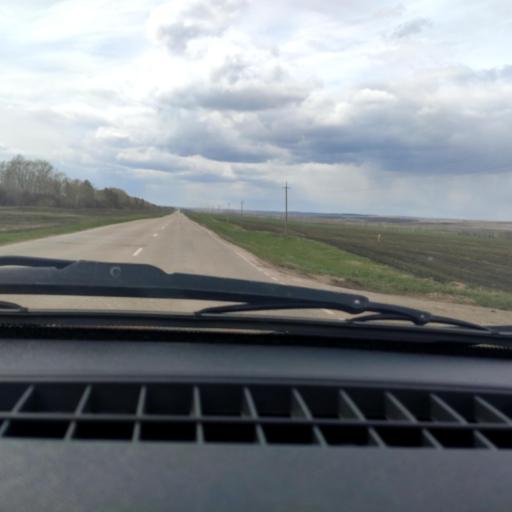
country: RU
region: Bashkortostan
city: Chekmagush
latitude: 55.1077
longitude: 54.9737
